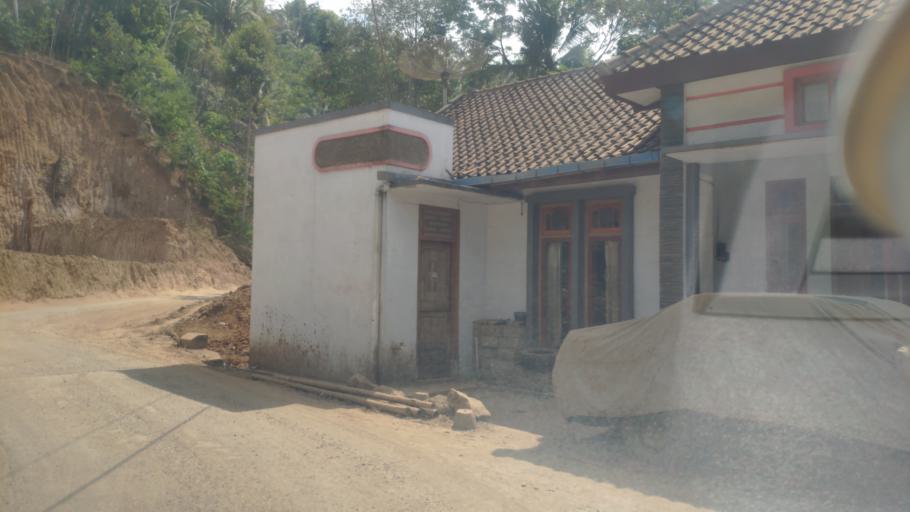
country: ID
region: Central Java
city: Wonosobo
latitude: -7.4402
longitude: 109.7008
